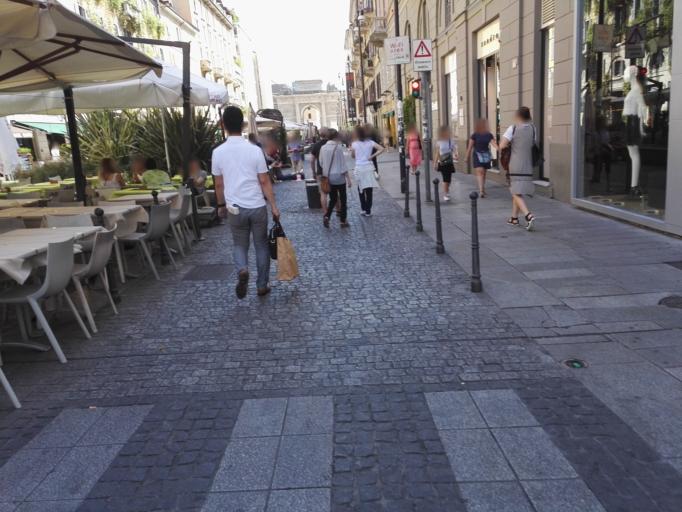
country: IT
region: Lombardy
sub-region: Citta metropolitana di Milano
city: Milano
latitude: 45.4823
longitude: 9.1872
